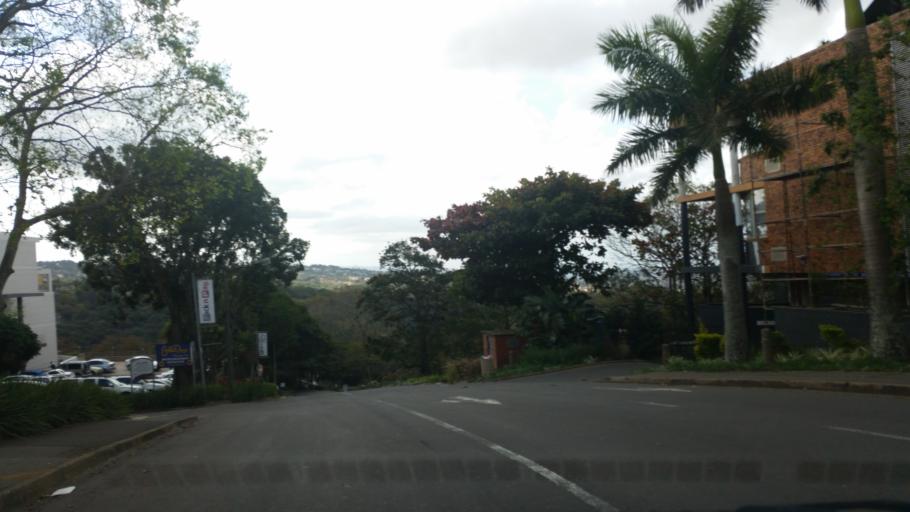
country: ZA
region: KwaZulu-Natal
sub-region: eThekwini Metropolitan Municipality
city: Berea
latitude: -29.8278
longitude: 30.9314
